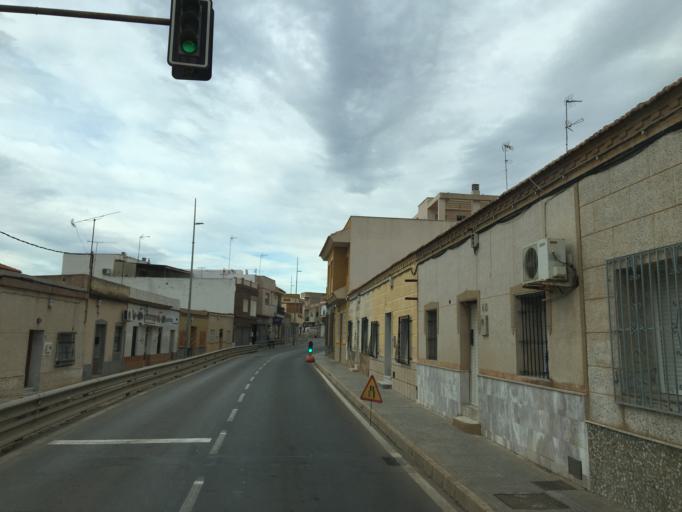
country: ES
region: Murcia
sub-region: Murcia
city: Cartagena
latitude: 37.6121
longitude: -1.0418
